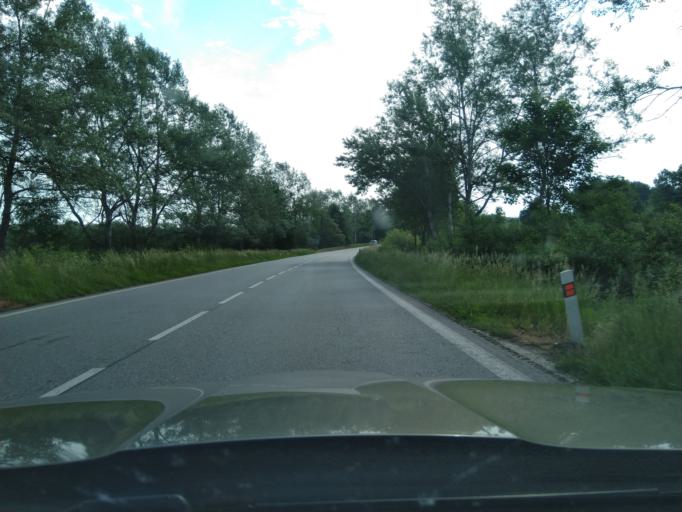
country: CZ
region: Jihocesky
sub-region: Okres Prachatice
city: Strunkovice nad Blanici
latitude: 49.0564
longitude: 14.0801
